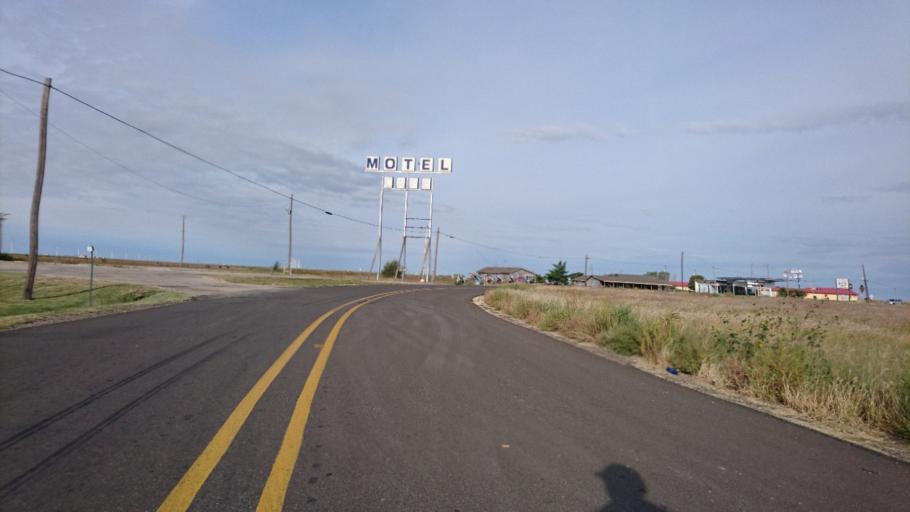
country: US
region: Texas
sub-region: Armstrong County
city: Claude
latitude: 35.2152
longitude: -101.3827
